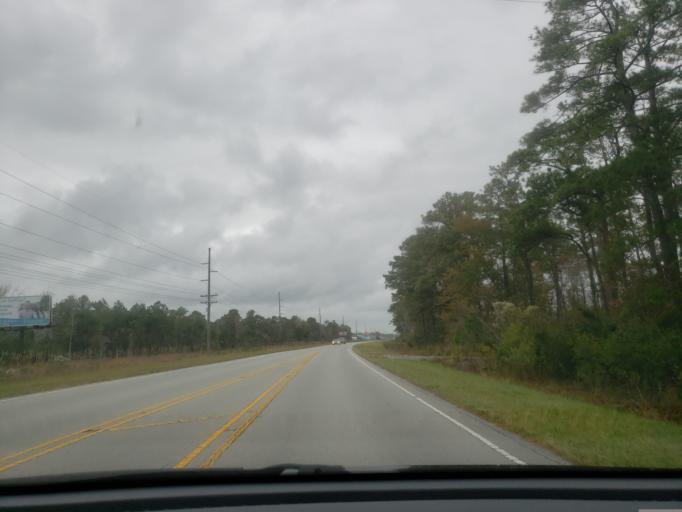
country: US
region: North Carolina
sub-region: Onslow County
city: Sneads Ferry
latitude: 34.5171
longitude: -77.4361
